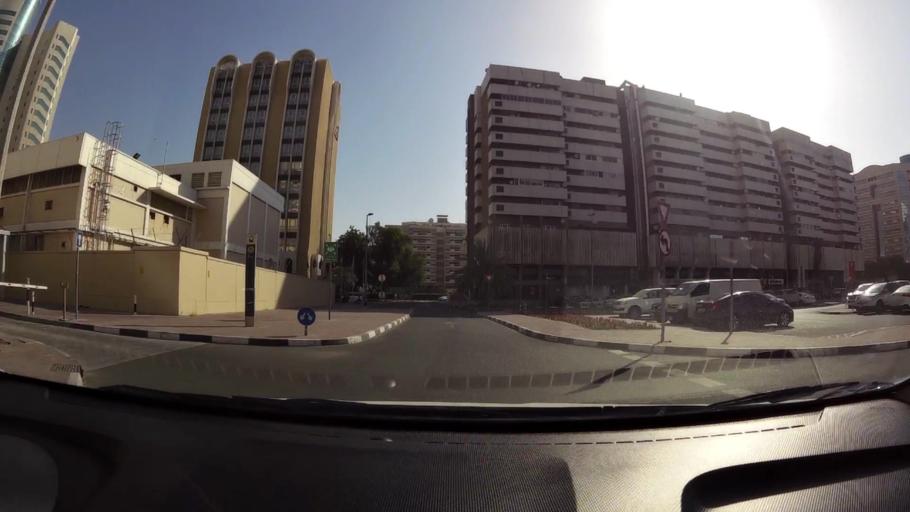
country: AE
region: Ash Shariqah
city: Sharjah
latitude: 25.2620
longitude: 55.3163
